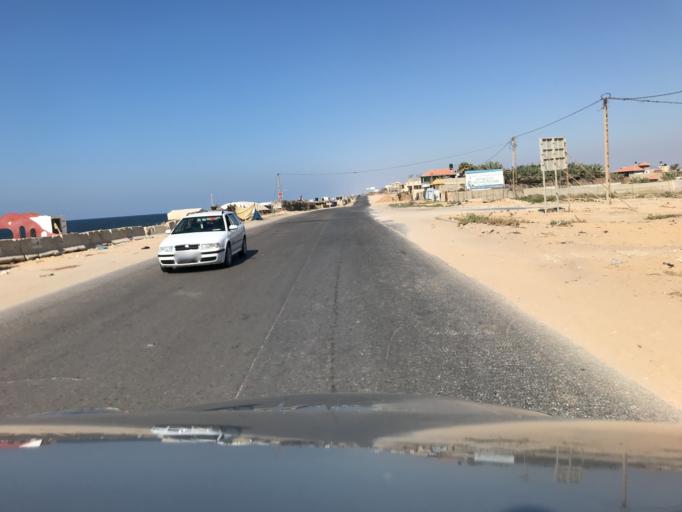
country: PS
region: Gaza Strip
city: Dayr al Balah
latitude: 31.4320
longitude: 34.3452
